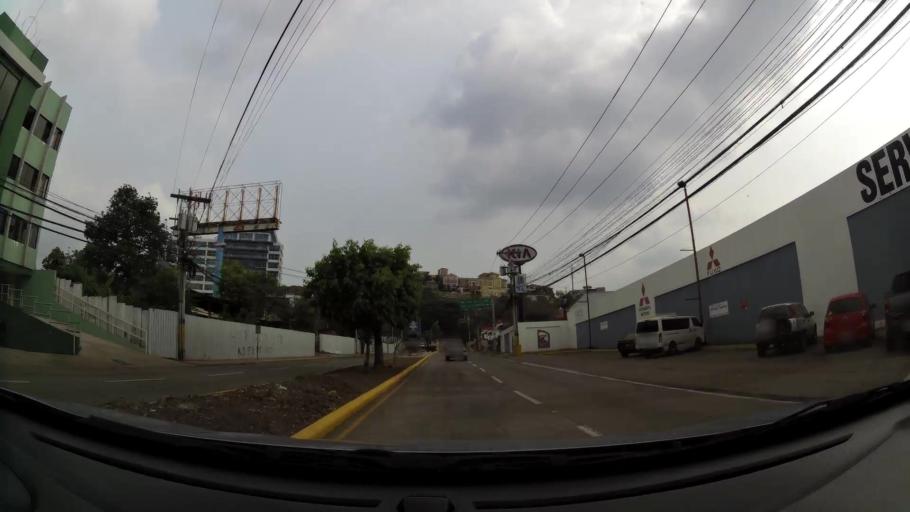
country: HN
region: Francisco Morazan
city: Tegucigalpa
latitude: 14.0878
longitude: -87.1740
